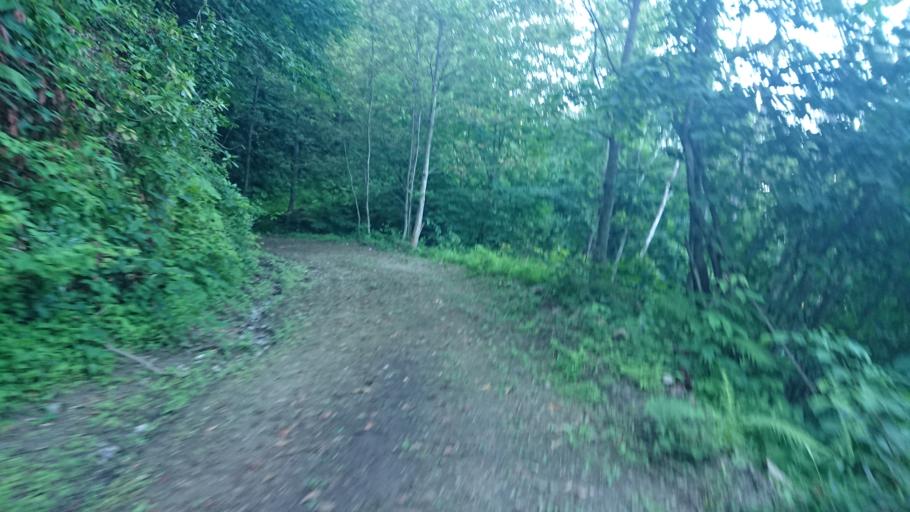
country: TR
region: Rize
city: Rize
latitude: 40.9736
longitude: 40.4971
